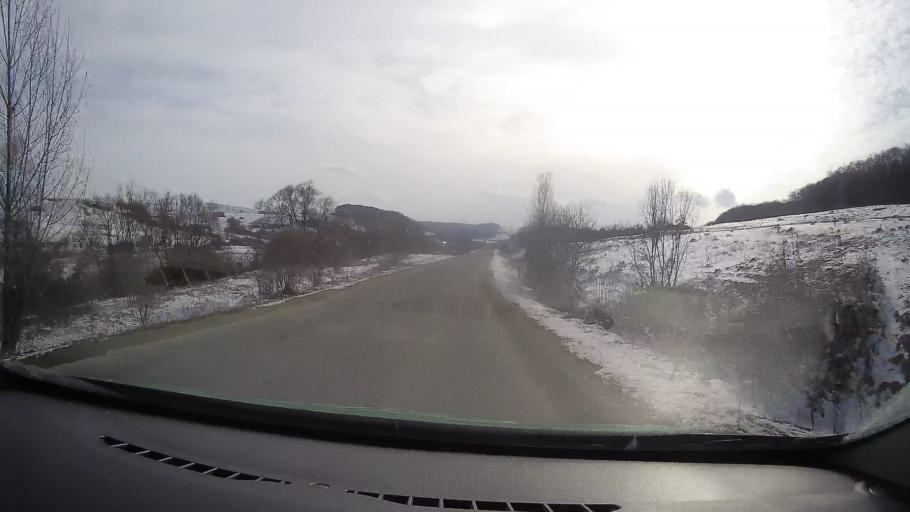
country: RO
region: Sibiu
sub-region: Comuna Bradeni
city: Bradeni
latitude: 46.0910
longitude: 24.8339
